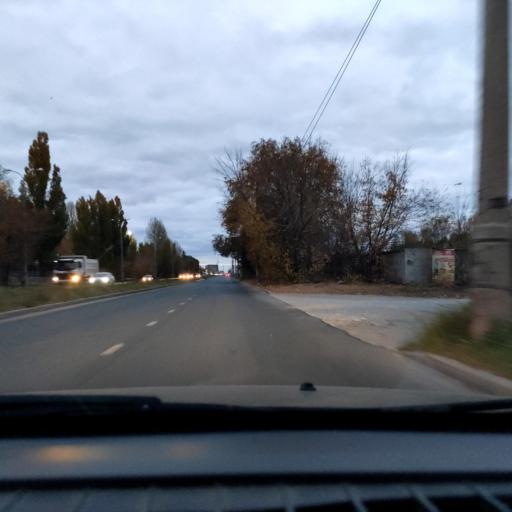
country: RU
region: Samara
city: Tol'yatti
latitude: 53.5556
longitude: 49.3038
